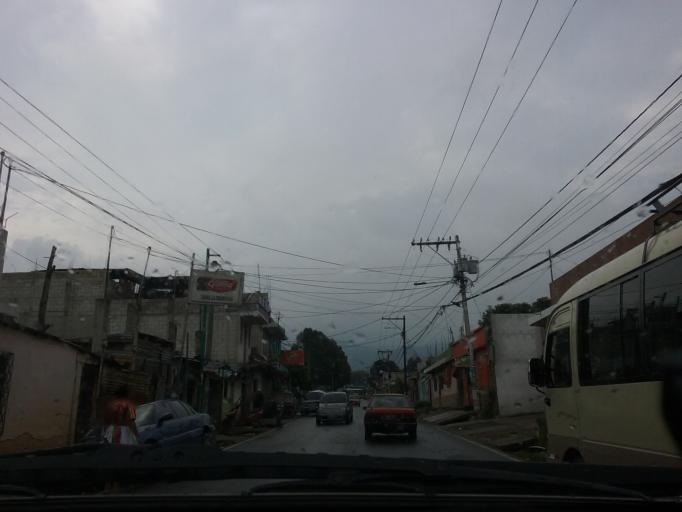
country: GT
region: Guatemala
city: Villa Nueva
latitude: 14.5443
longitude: -90.6134
